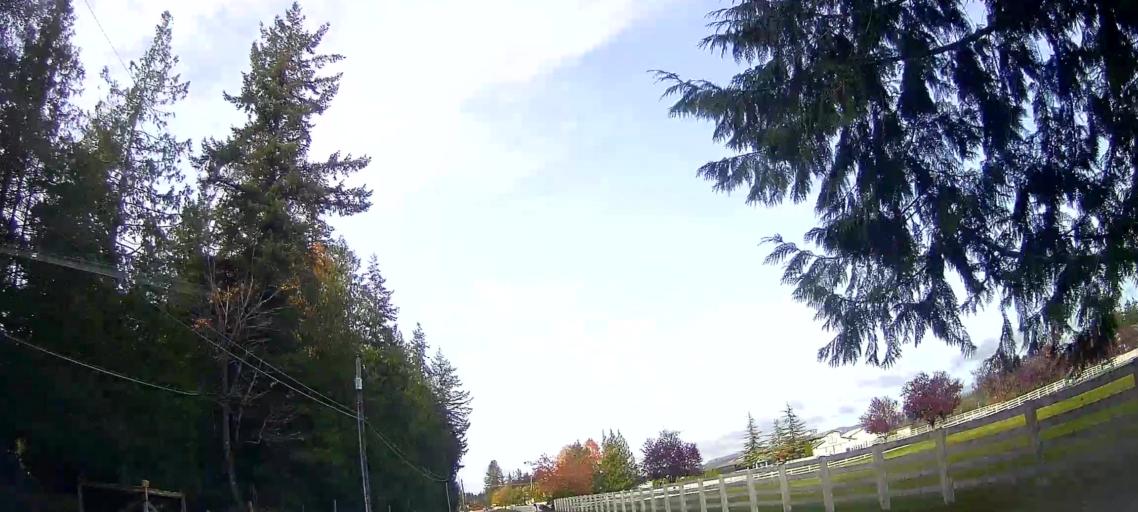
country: US
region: Washington
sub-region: Snohomish County
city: Stanwood
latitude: 48.2658
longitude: -122.3414
